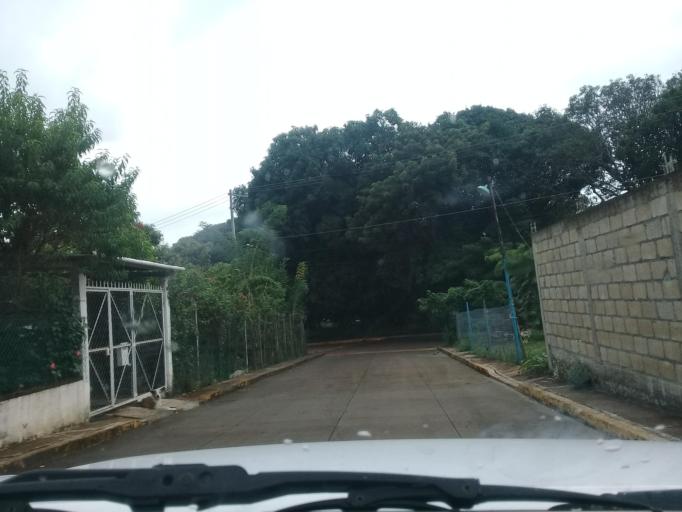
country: MX
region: Veracruz
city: San Andres Tuxtla
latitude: 18.4357
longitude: -95.2105
